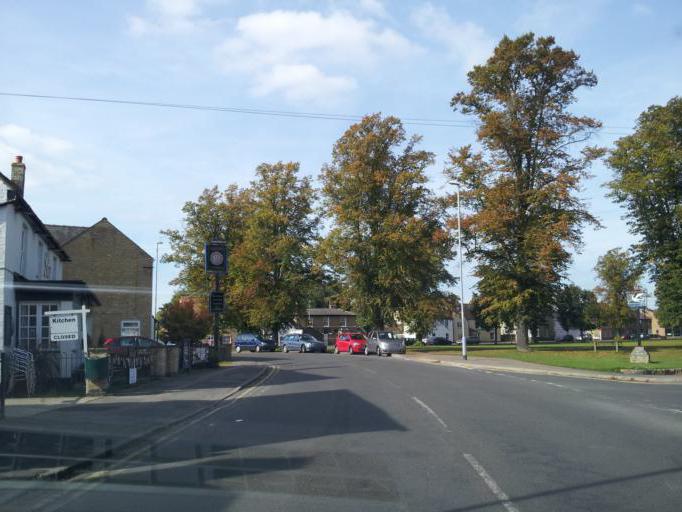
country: GB
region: England
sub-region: Cambridgeshire
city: Waterbeach
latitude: 52.2655
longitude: 0.1912
